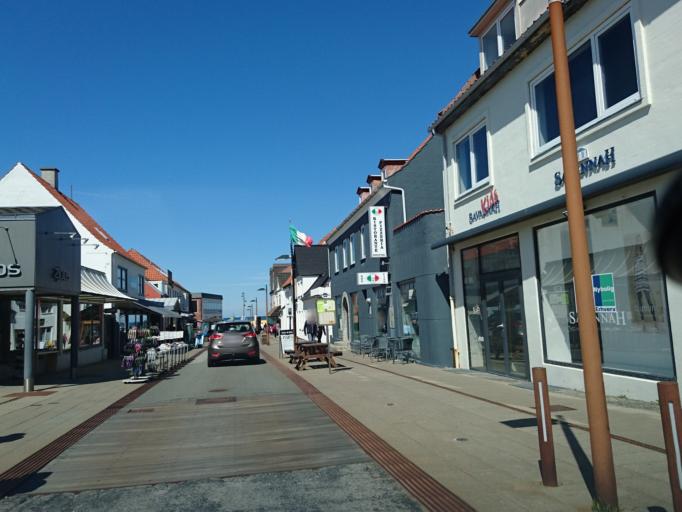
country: DK
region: North Denmark
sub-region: Hjorring Kommune
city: Hirtshals
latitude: 57.5899
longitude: 9.9575
